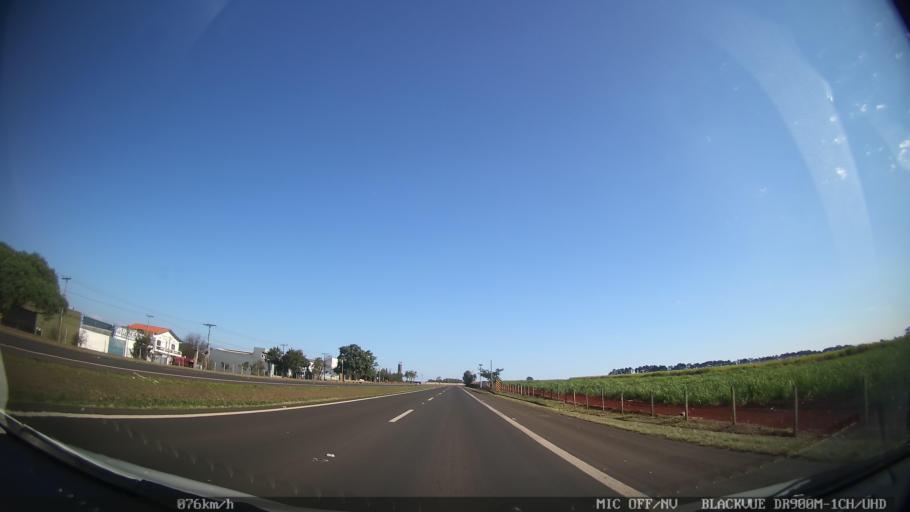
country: BR
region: Sao Paulo
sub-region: Piracicaba
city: Piracicaba
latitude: -22.6846
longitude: -47.6387
